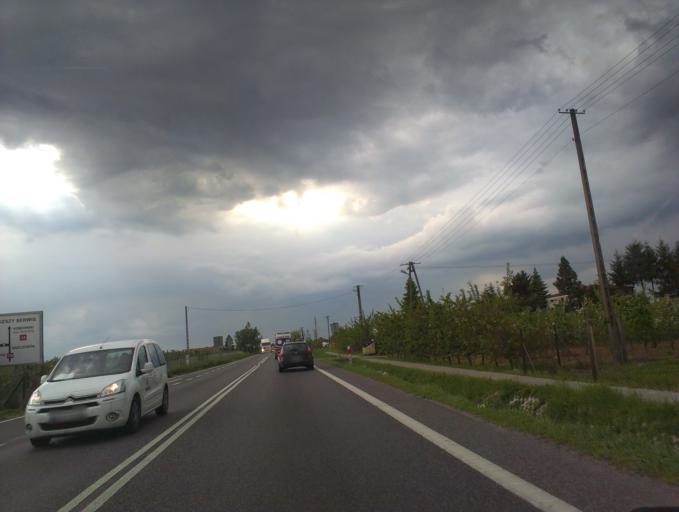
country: PL
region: Masovian Voivodeship
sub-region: Powiat grojecki
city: Pniewy
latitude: 51.9098
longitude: 20.7355
